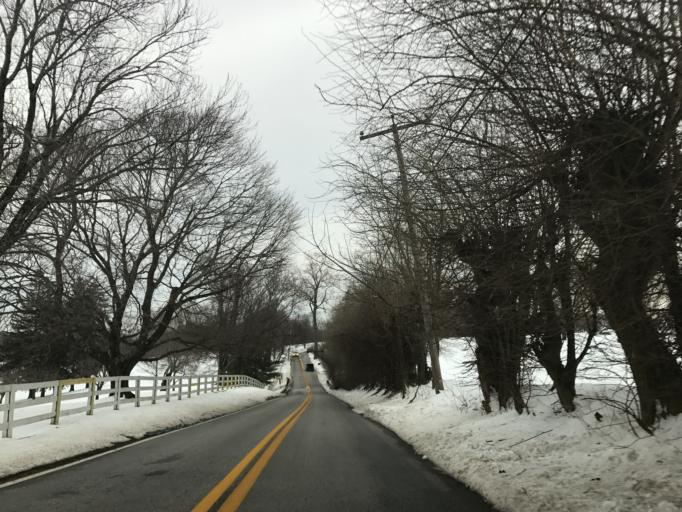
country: US
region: Maryland
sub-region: Baltimore County
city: Mays Chapel
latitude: 39.4429
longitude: -76.6625
